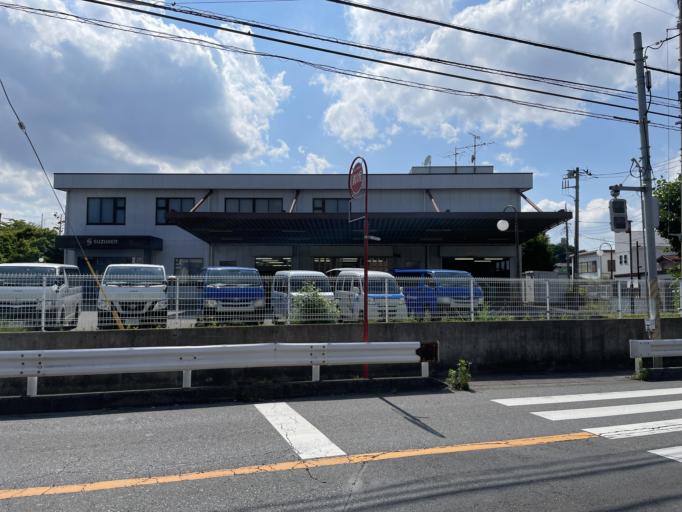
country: JP
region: Chiba
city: Kashiwa
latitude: 35.8051
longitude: 139.9634
